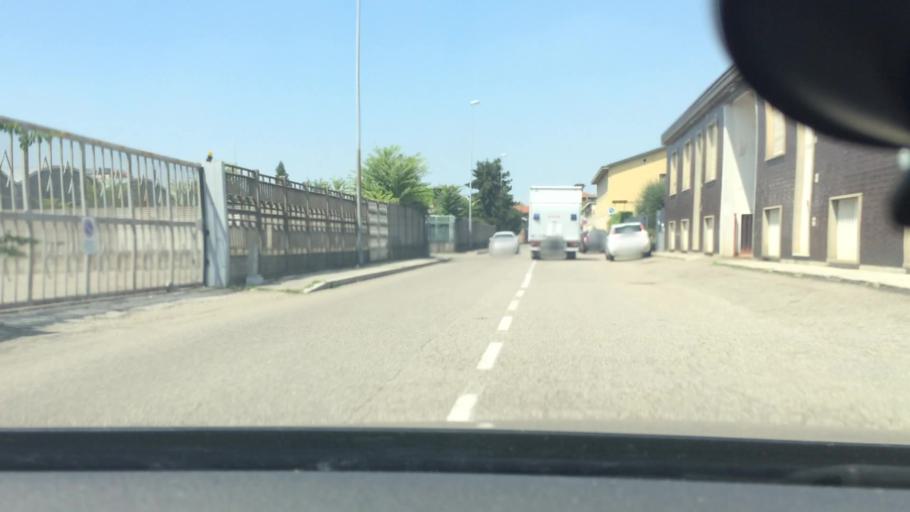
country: IT
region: Lombardy
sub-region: Citta metropolitana di Milano
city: Pero
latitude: 45.5046
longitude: 9.0865
